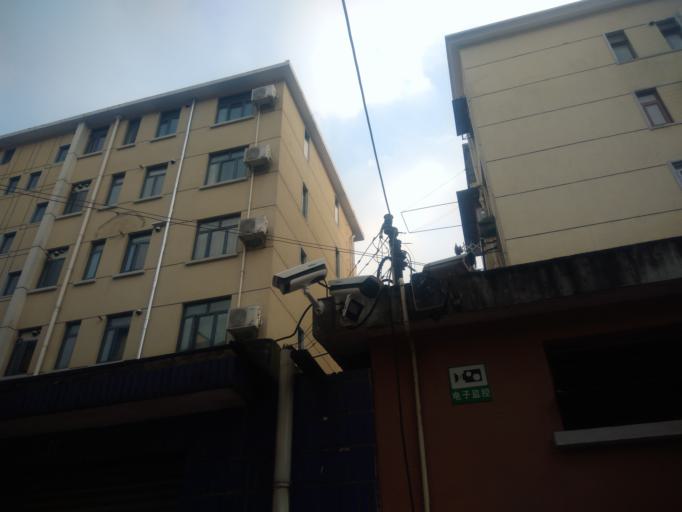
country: CN
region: Shanghai Shi
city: Changning
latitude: 31.2110
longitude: 121.3949
